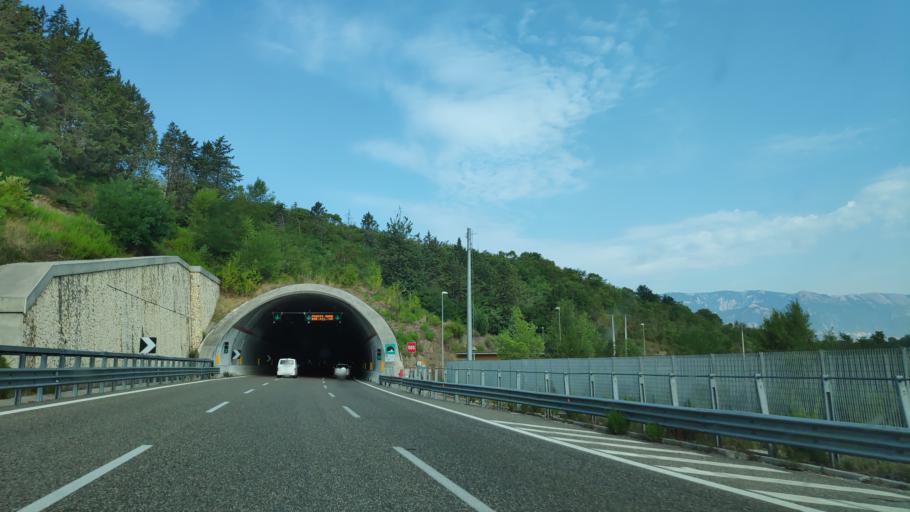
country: IT
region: Campania
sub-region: Provincia di Salerno
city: Contursi Terme
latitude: 40.6132
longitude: 15.2514
